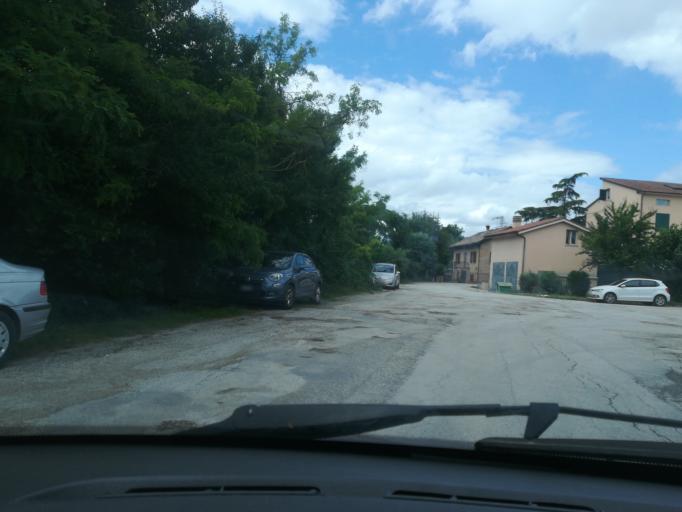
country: IT
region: The Marches
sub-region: Provincia di Macerata
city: Sforzacosta
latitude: 43.2577
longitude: 13.4276
